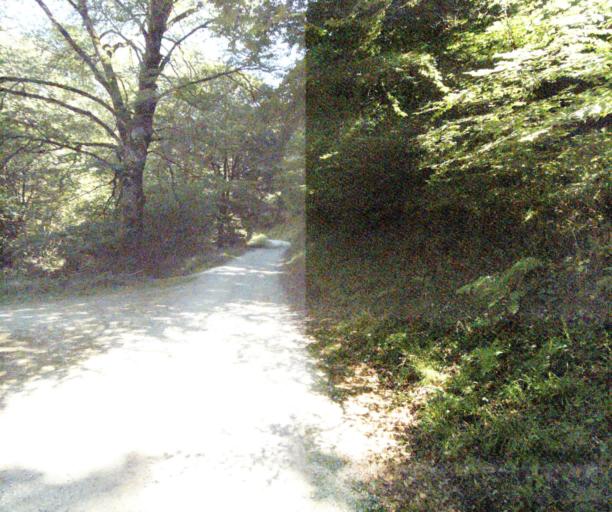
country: FR
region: Midi-Pyrenees
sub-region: Departement du Tarn
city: Soreze
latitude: 43.4387
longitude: 2.0886
